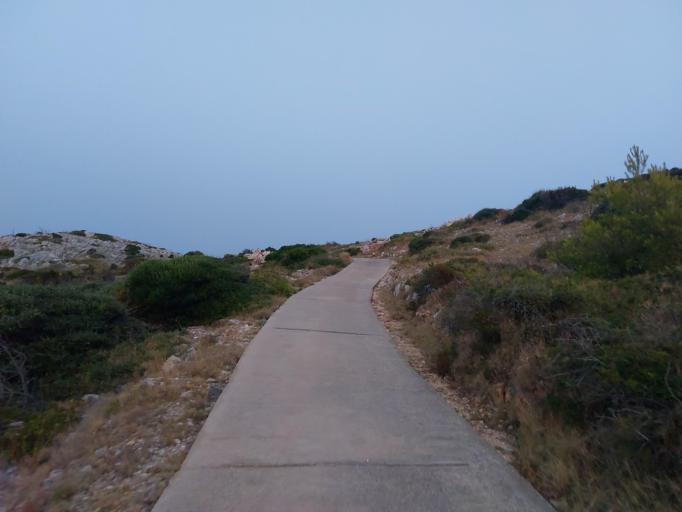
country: HR
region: Dubrovacko-Neretvanska
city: Smokvica
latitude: 42.7253
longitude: 16.8856
